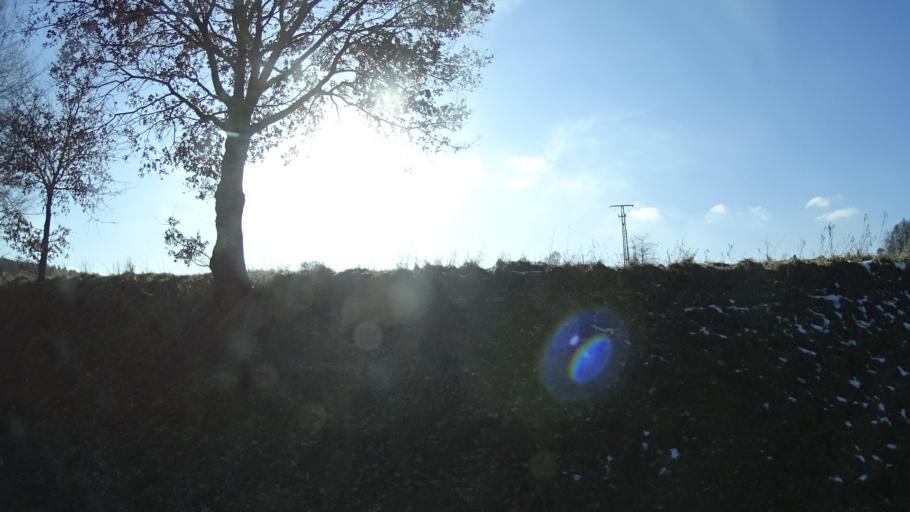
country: DE
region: Bavaria
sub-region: Regierungsbezirk Unterfranken
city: Motten
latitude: 50.4363
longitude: 9.7346
